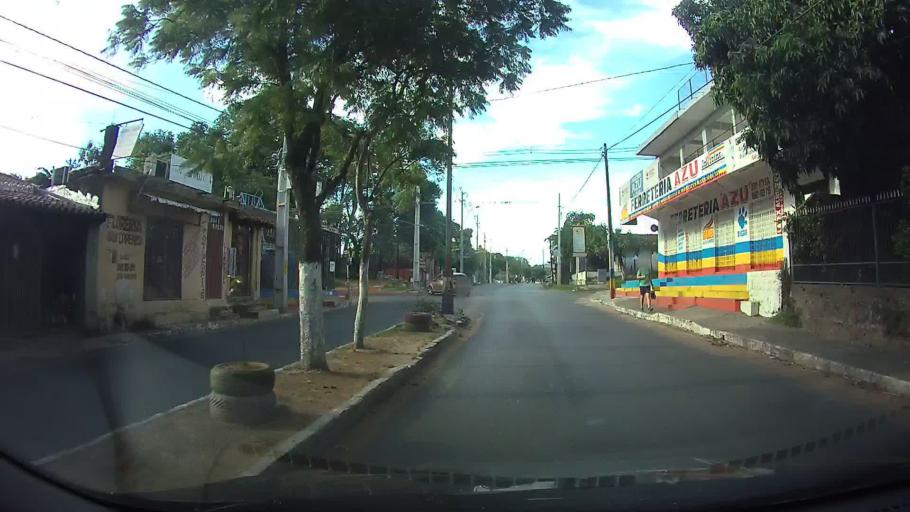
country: PY
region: Central
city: San Antonio
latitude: -25.4122
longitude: -57.5739
